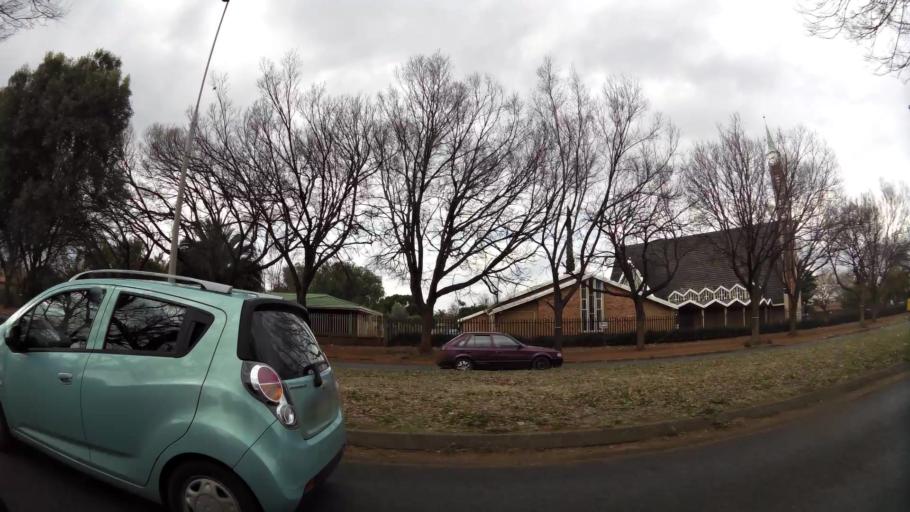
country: ZA
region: Gauteng
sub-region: Sedibeng District Municipality
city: Vanderbijlpark
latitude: -26.7046
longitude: 27.8239
